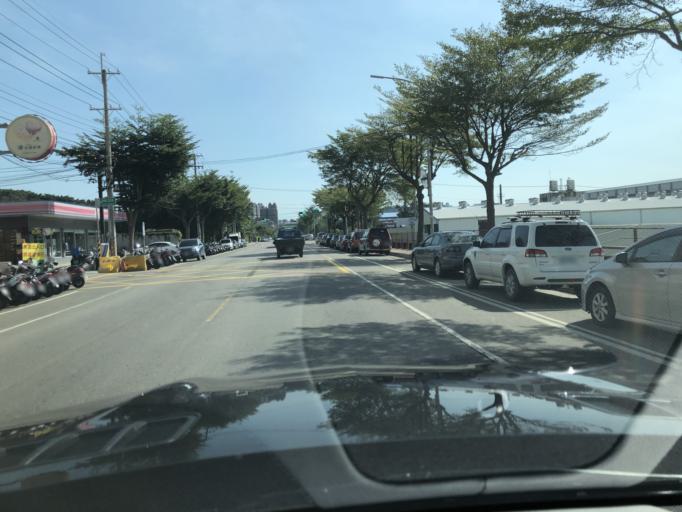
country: TW
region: Taiwan
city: Taoyuan City
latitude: 25.0669
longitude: 121.2904
